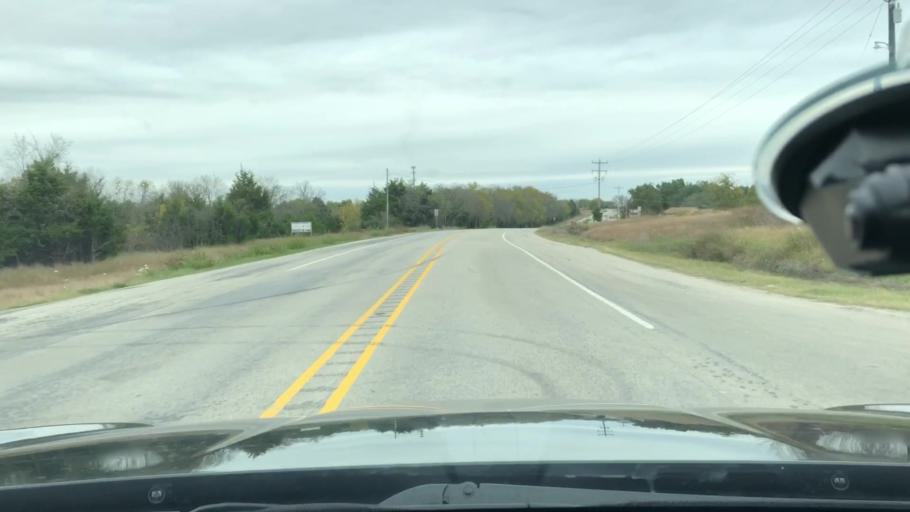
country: US
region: Texas
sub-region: Hunt County
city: Greenville
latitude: 33.0621
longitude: -96.1099
